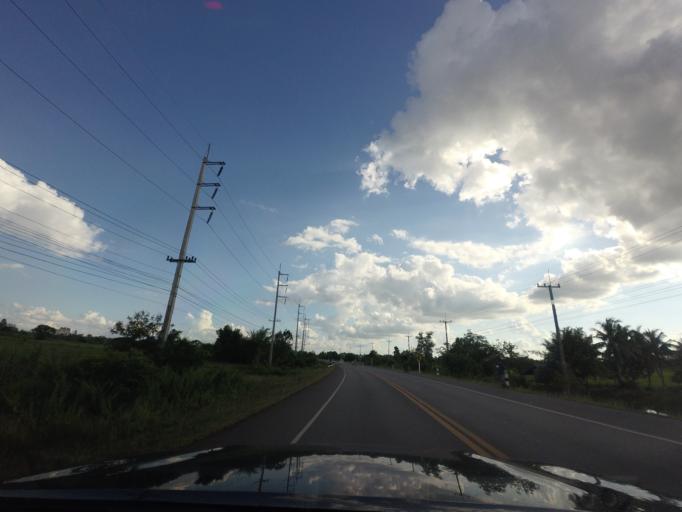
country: TH
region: Changwat Udon Thani
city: Thung Fon
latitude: 17.5144
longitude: 103.2039
